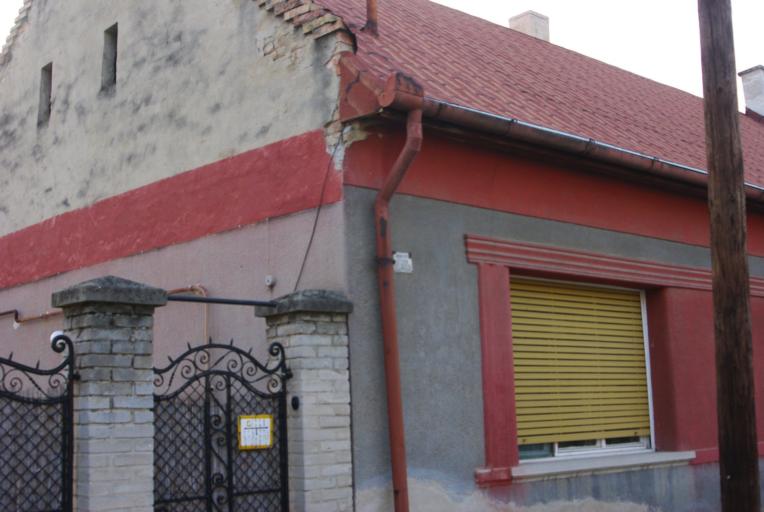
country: HU
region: Pest
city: Fot
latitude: 47.6143
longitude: 19.1947
